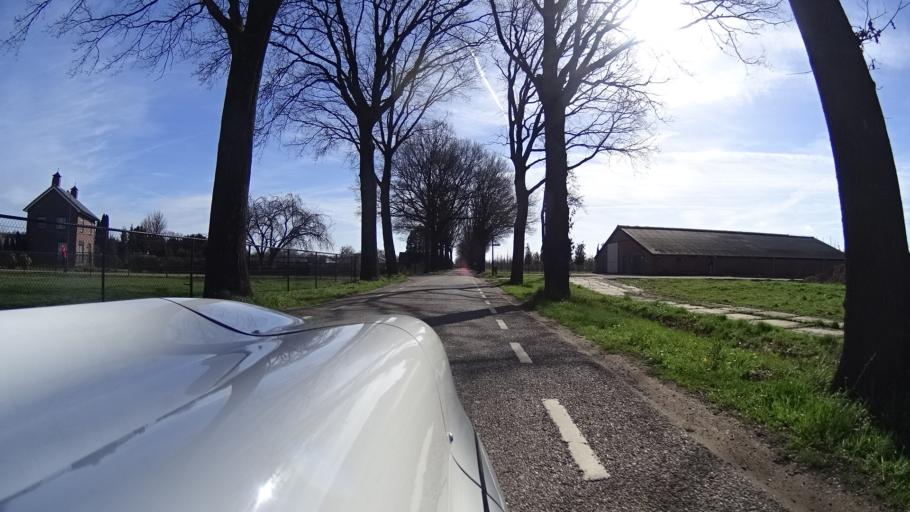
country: NL
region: North Brabant
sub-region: Gemeente Cuijk
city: Cuijk
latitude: 51.7115
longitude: 5.8505
